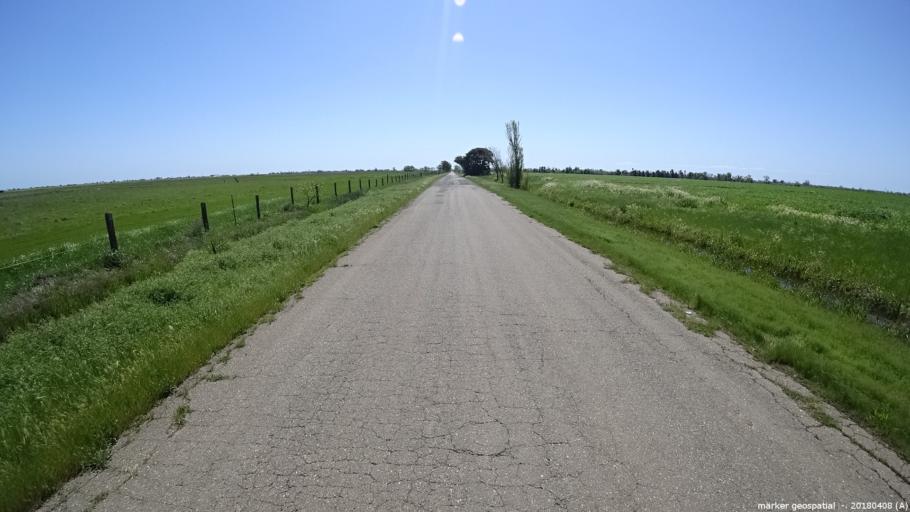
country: US
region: California
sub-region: Sacramento County
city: Laguna
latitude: 38.3713
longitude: -121.4821
